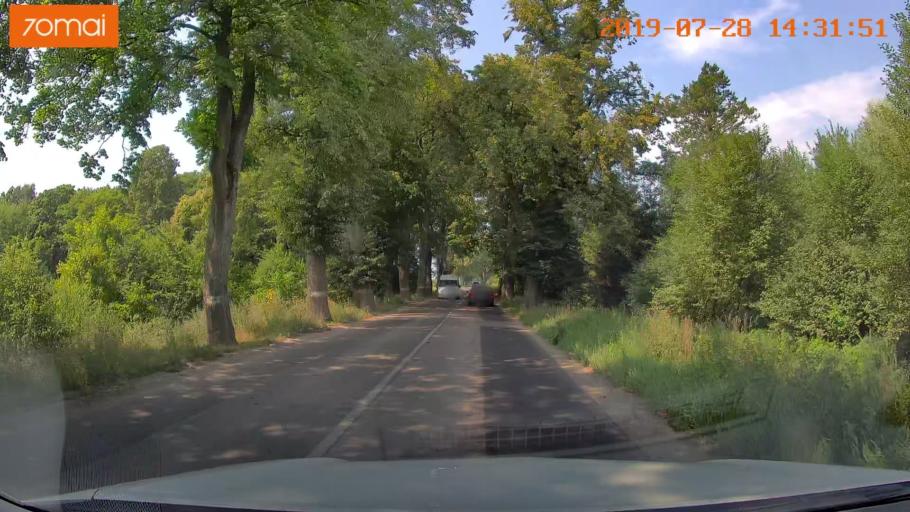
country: RU
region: Kaliningrad
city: Primorsk
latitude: 54.8089
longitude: 20.0477
